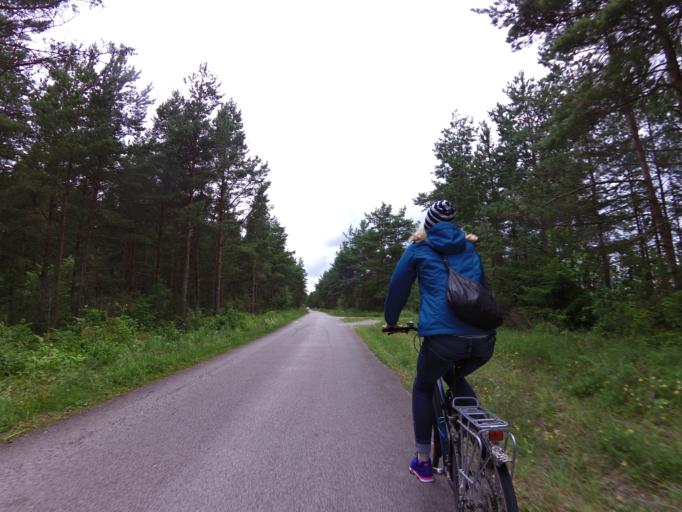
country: EE
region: Laeaene
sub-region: Vormsi vald
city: Hullo
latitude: 58.9793
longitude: 23.2536
